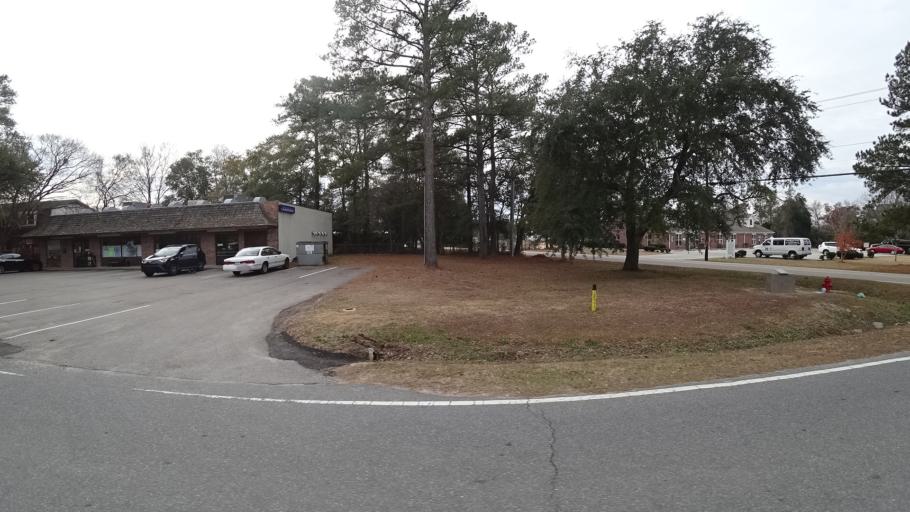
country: US
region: North Carolina
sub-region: Moore County
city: Pinehurst
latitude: 35.2022
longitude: -79.4669
